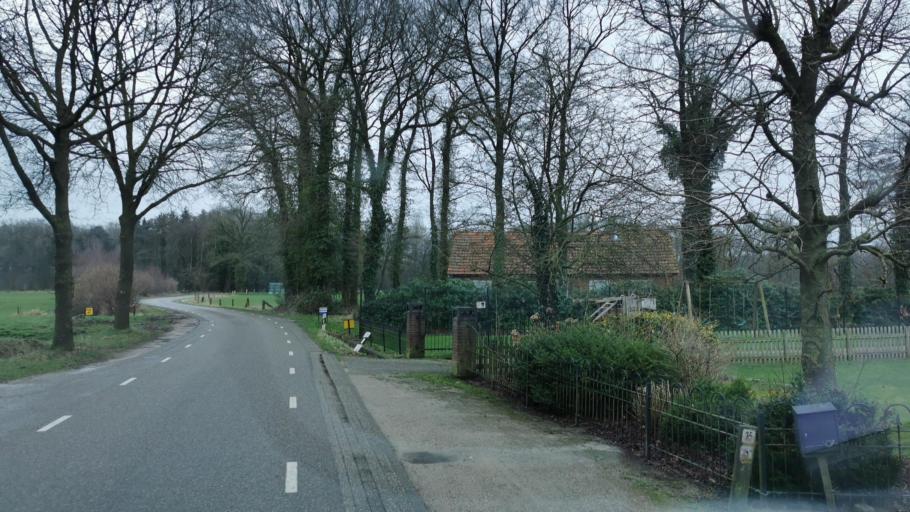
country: NL
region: Overijssel
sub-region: Gemeente Hengelo
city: Hengelo
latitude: 52.3332
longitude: 6.8159
